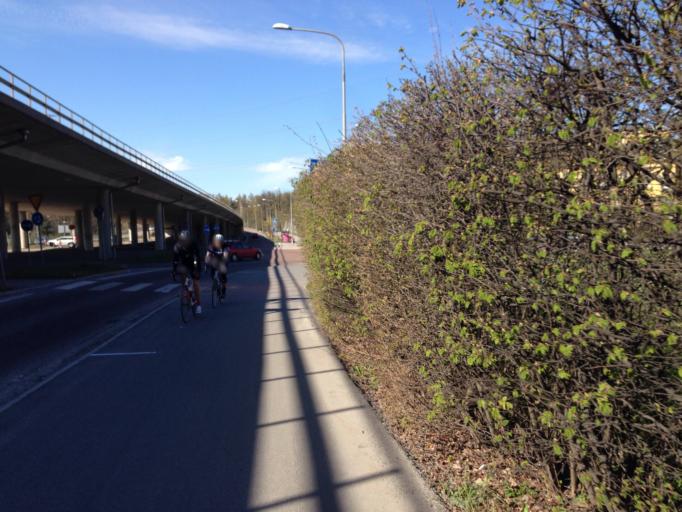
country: SE
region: Stockholm
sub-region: Norrtalje Kommun
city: Bergshamra
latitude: 59.3701
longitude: 18.0512
